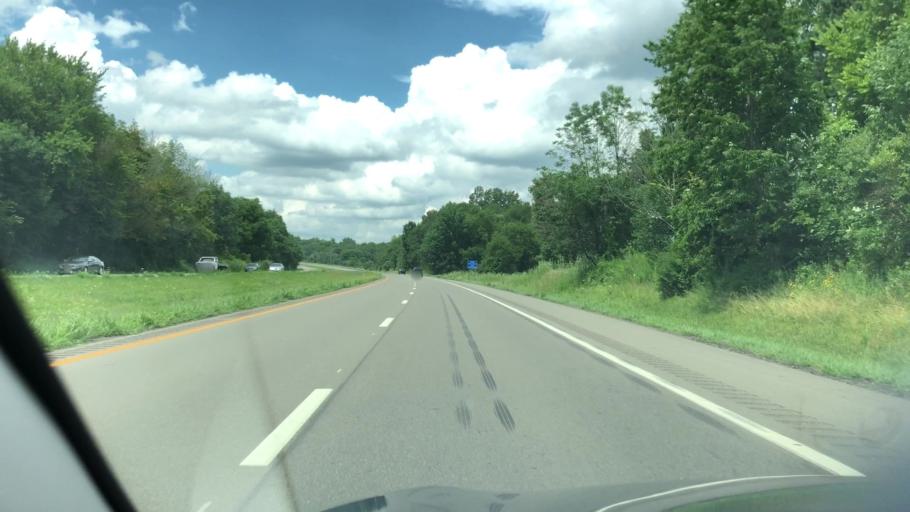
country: US
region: Ohio
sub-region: Stark County
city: Canal Fulton
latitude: 40.8608
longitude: -81.5809
